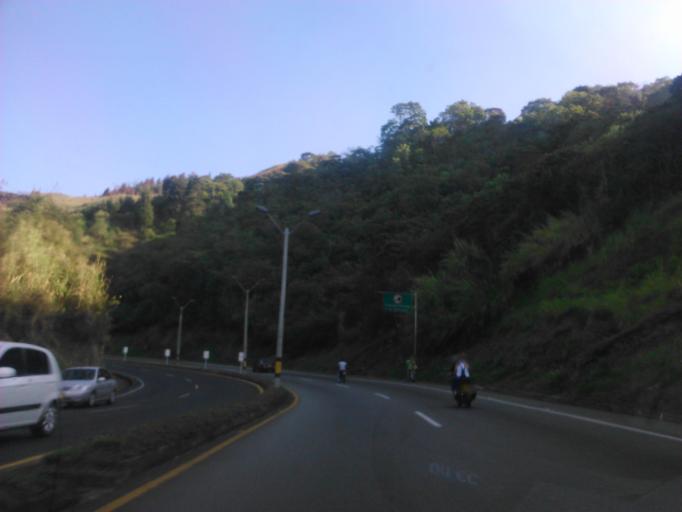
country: CO
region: Antioquia
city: Municipio de Copacabana
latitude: 6.3255
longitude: -75.5118
